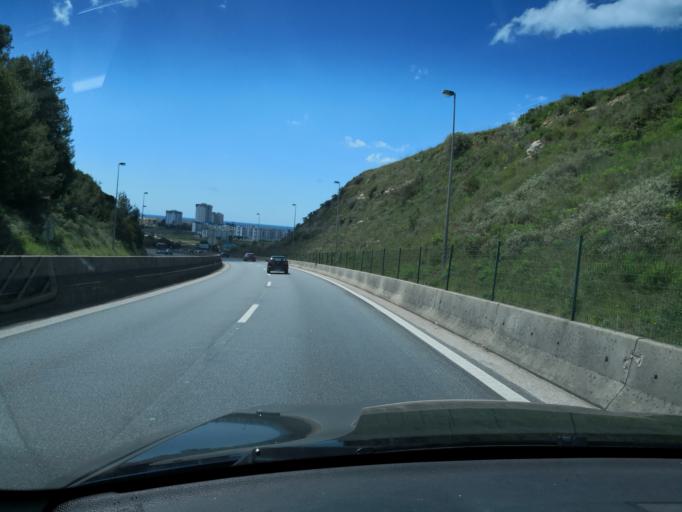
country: PT
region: Setubal
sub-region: Almada
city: Costa de Caparica
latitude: 38.6506
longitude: -9.2284
